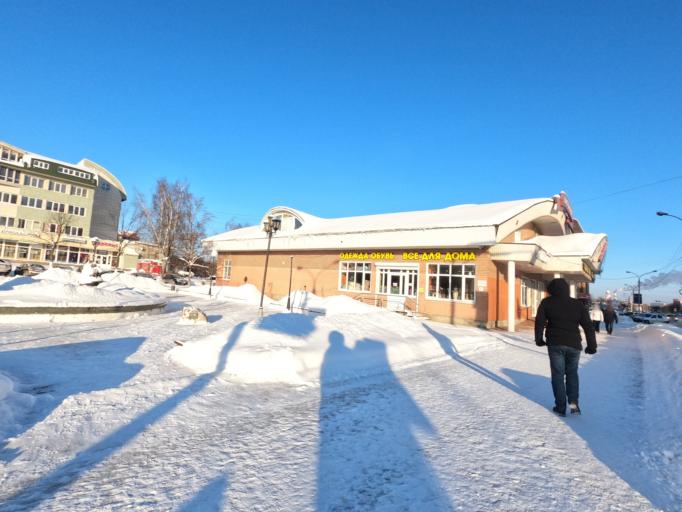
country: RU
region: Moskovskaya
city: Dmitrov
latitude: 56.3491
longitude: 37.5197
